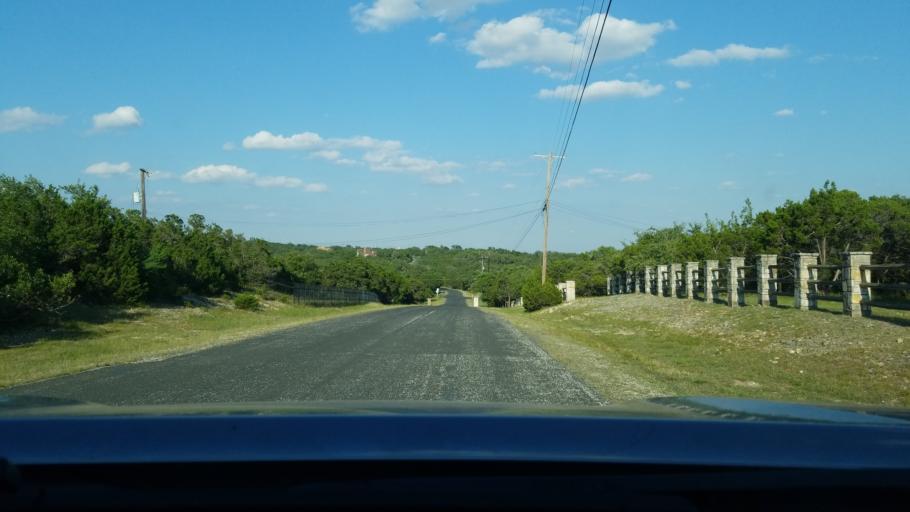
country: US
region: Texas
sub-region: Bexar County
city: Timberwood Park
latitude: 29.7054
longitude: -98.4403
